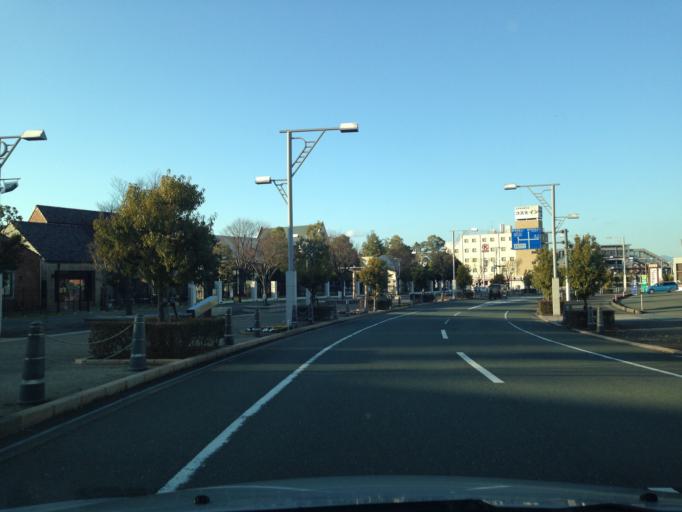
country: JP
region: Shizuoka
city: Fukuroi
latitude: 34.7492
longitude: 137.9626
